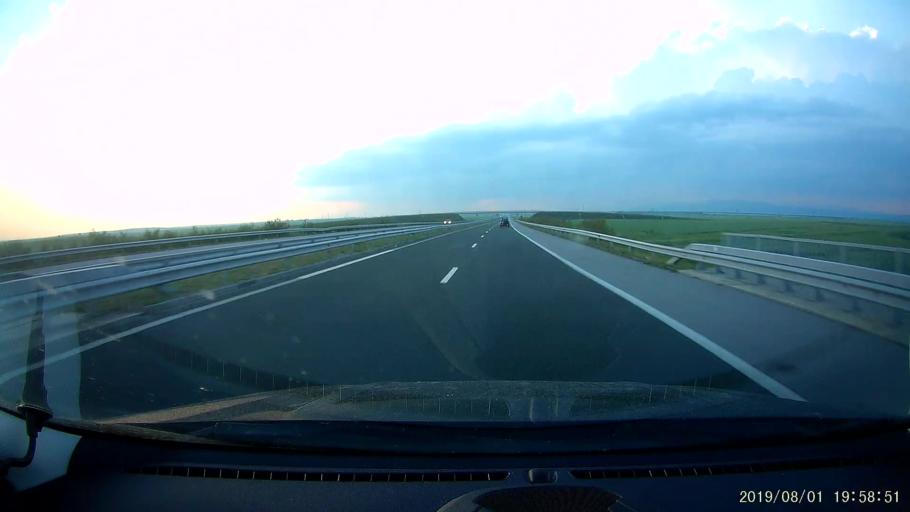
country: BG
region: Yambol
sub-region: Obshtina Straldzha
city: Straldzha
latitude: 42.5466
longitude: 26.7508
